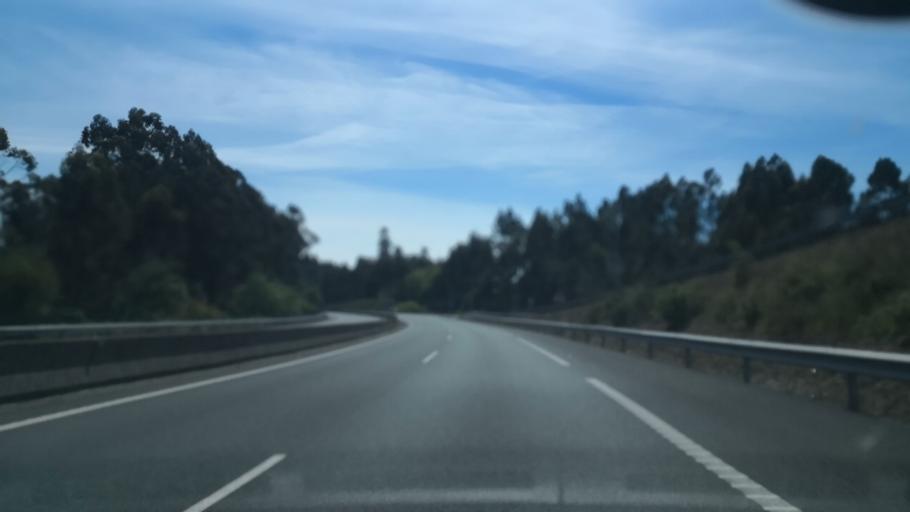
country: ES
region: Galicia
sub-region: Provincia de Pontevedra
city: Portas
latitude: 42.5977
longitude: -8.6756
